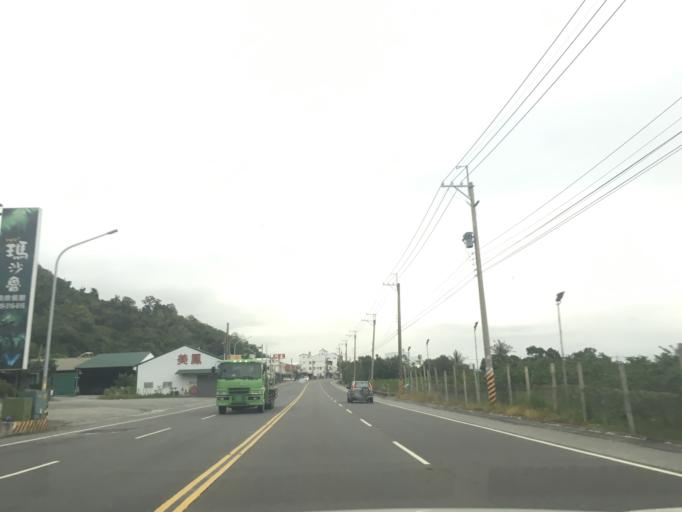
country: TW
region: Taiwan
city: Taitung City
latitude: 22.6821
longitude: 121.0428
